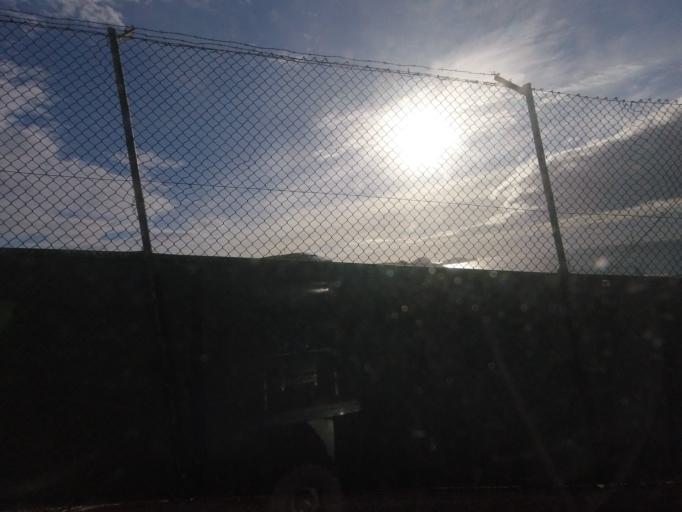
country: PT
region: Madeira
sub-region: Machico
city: Canical
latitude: 32.7431
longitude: -16.7379
